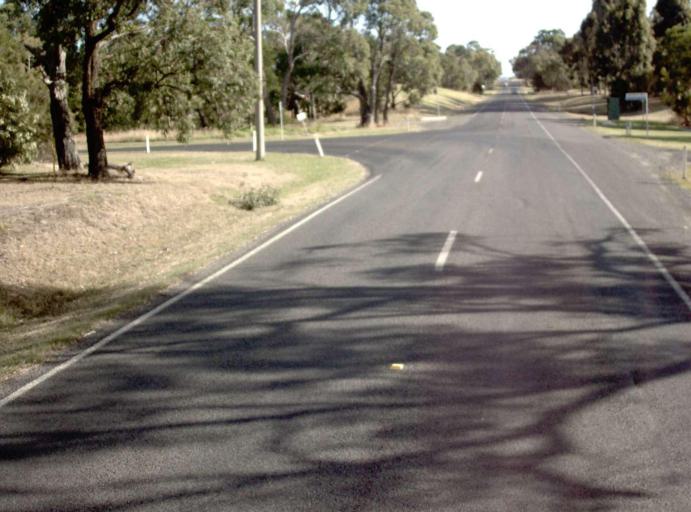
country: AU
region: Victoria
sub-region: Latrobe
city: Morwell
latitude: -38.3010
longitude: 146.4219
